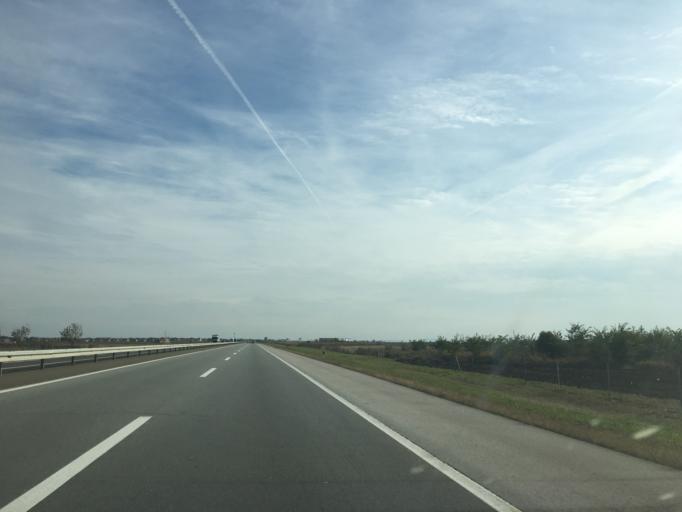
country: RS
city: Novi Banovci
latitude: 44.9580
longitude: 20.2552
